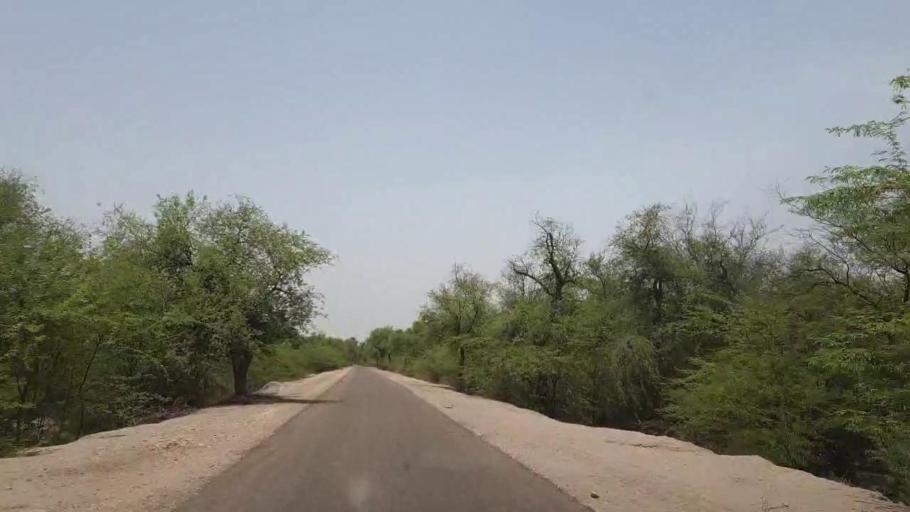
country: PK
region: Sindh
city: Sakrand
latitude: 26.1017
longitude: 68.2509
